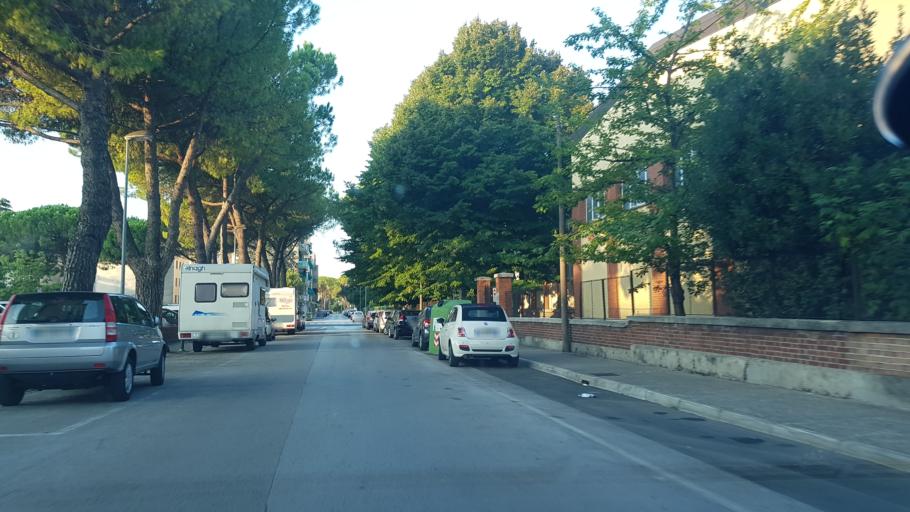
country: IT
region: Friuli Venezia Giulia
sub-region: Provincia di Gorizia
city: Monfalcone
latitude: 45.8077
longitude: 13.5377
